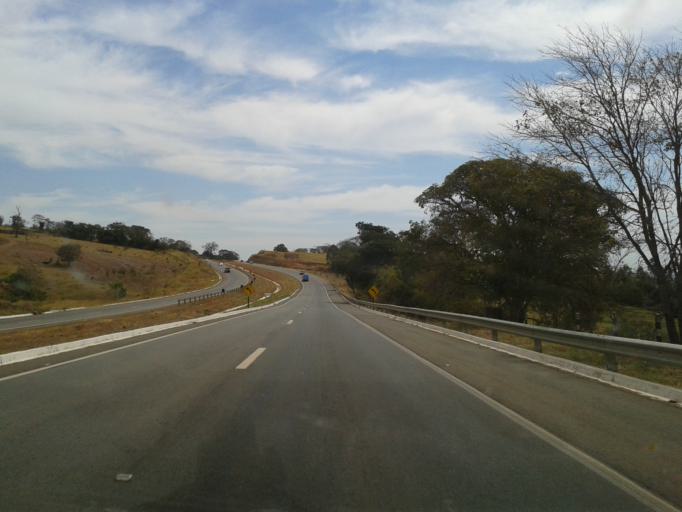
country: BR
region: Goias
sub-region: Itaberai
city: Itaberai
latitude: -16.1504
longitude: -49.6316
